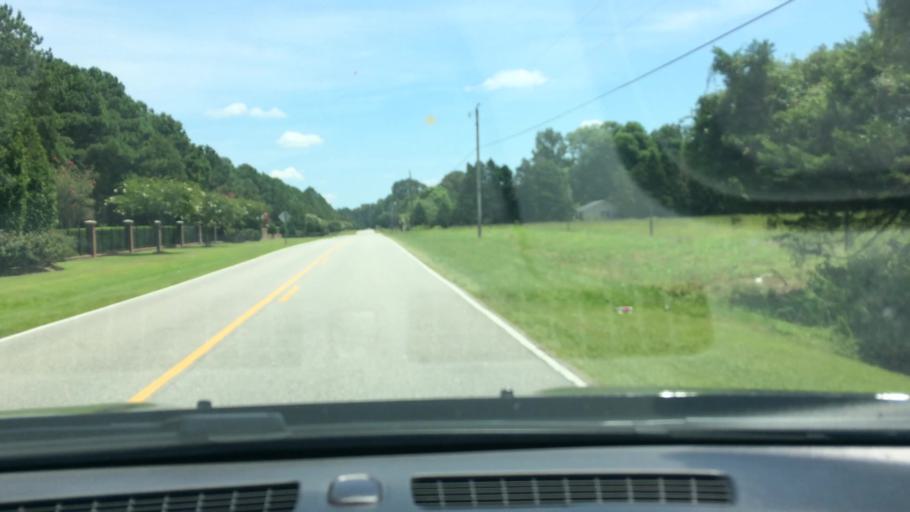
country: US
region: North Carolina
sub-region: Pitt County
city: Windsor
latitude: 35.5578
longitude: -77.2445
